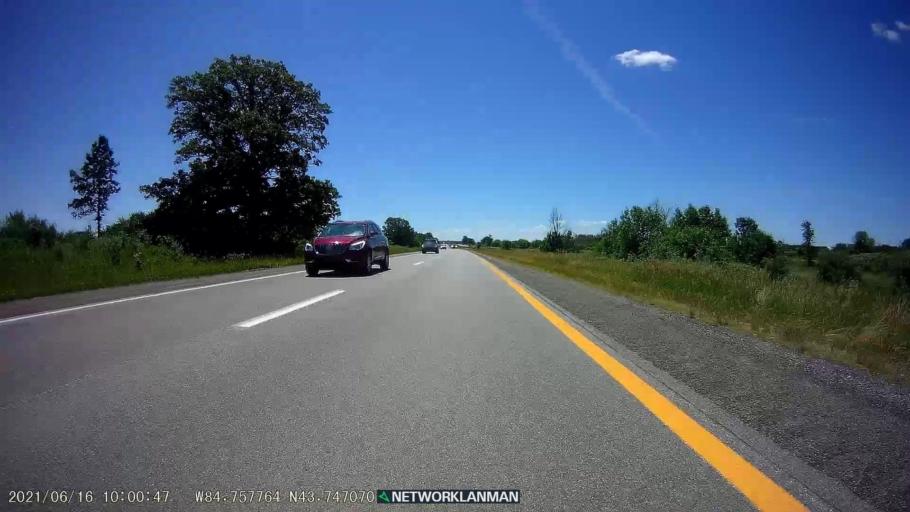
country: US
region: Michigan
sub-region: Clare County
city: Clare
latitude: 43.7475
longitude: -84.7577
